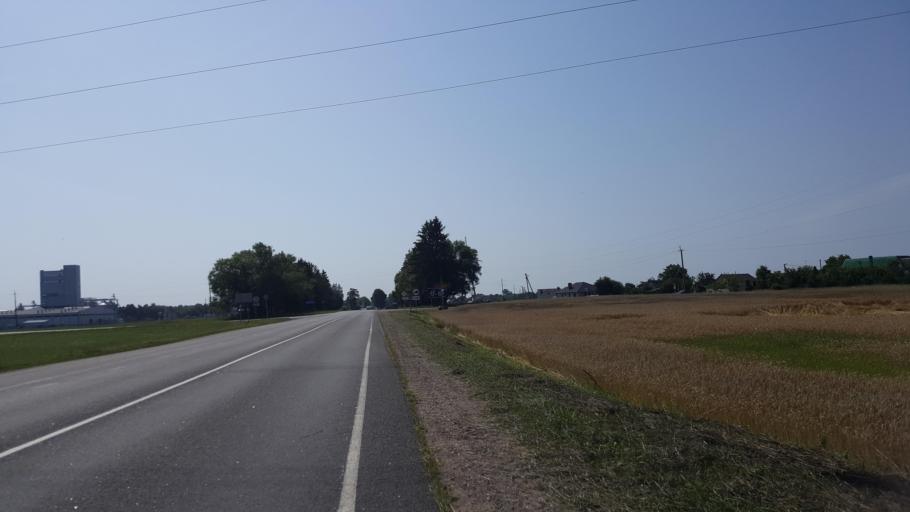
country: BY
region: Brest
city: Zhabinka
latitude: 52.2122
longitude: 23.9993
